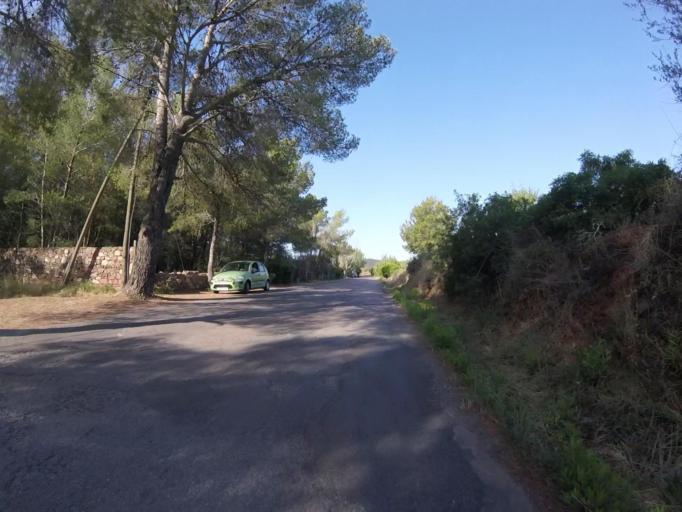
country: ES
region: Valencia
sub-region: Provincia de Castello
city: Benicassim
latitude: 40.0764
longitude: 0.0465
